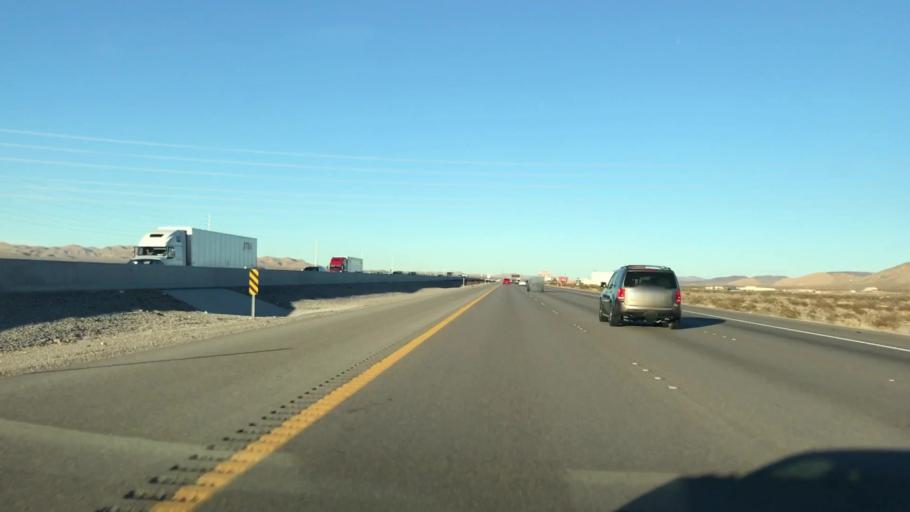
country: US
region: Nevada
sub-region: Clark County
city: Enterprise
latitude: 35.7624
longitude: -115.3423
